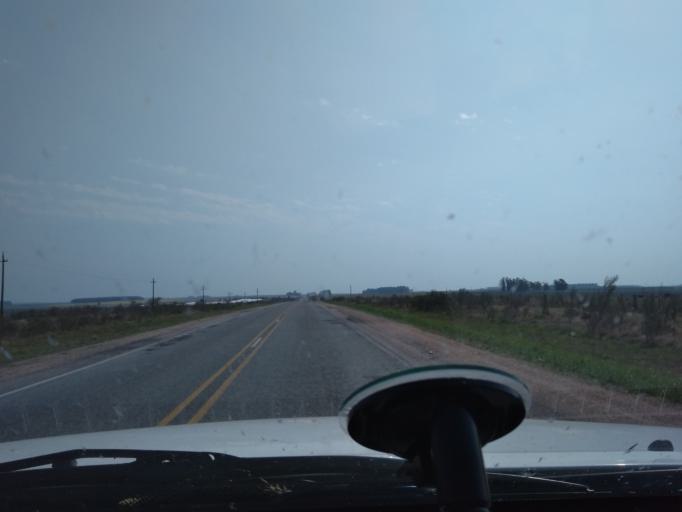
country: UY
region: Canelones
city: San Ramon
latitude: -34.0416
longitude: -55.9445
